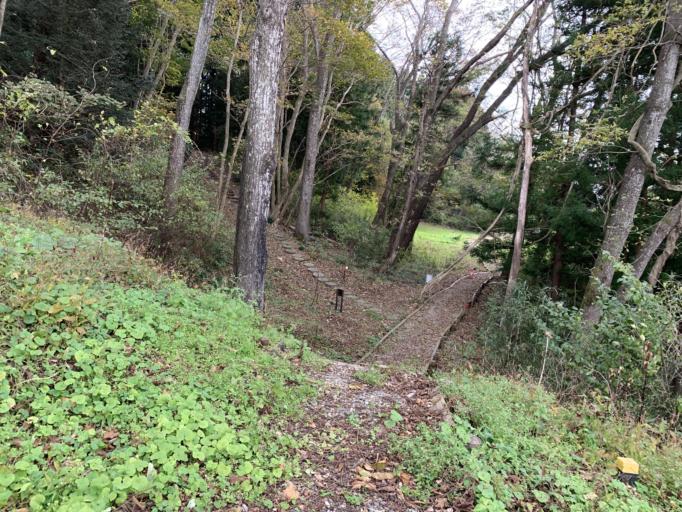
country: JP
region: Iwate
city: Mizusawa
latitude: 39.0265
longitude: 141.1351
